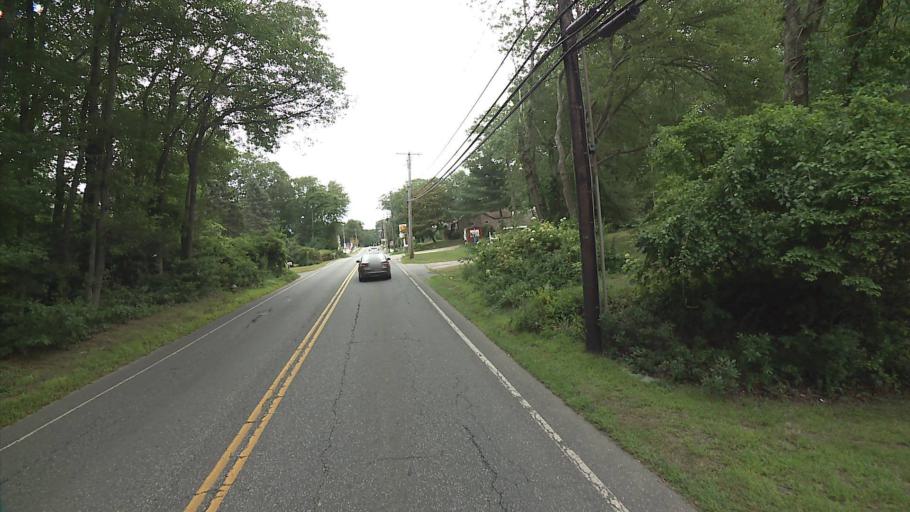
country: US
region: Connecticut
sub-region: New London County
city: Niantic
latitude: 41.3188
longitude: -72.2285
